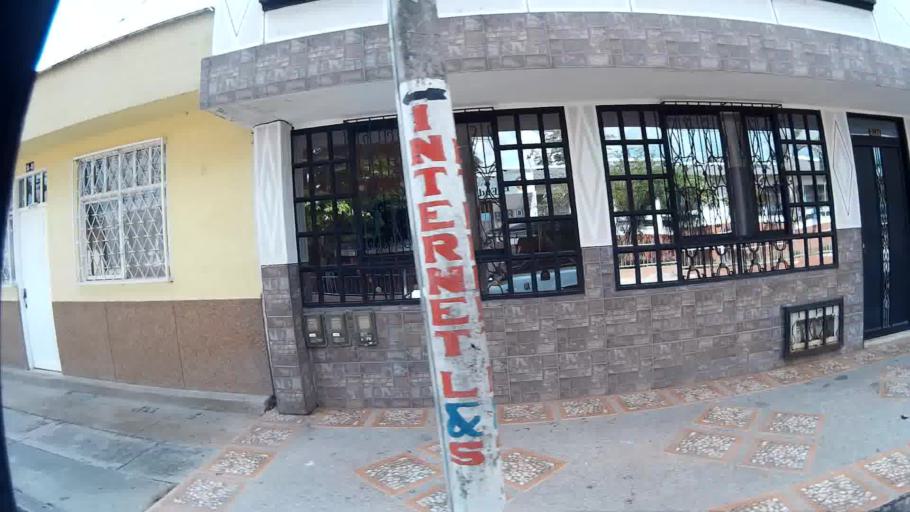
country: CO
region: Quindio
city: Armenia
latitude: 4.5433
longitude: -75.6691
